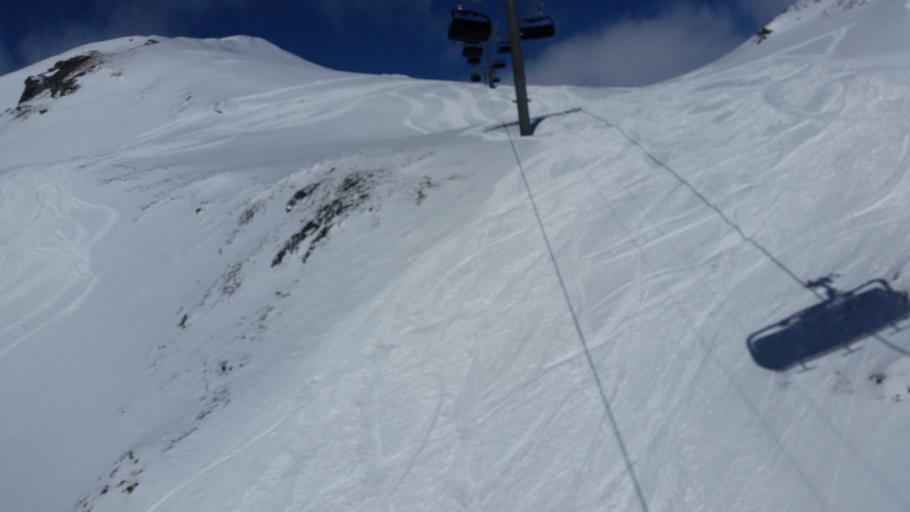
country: CH
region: Grisons
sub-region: Surselva District
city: Ilanz
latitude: 46.8567
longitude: 9.1662
